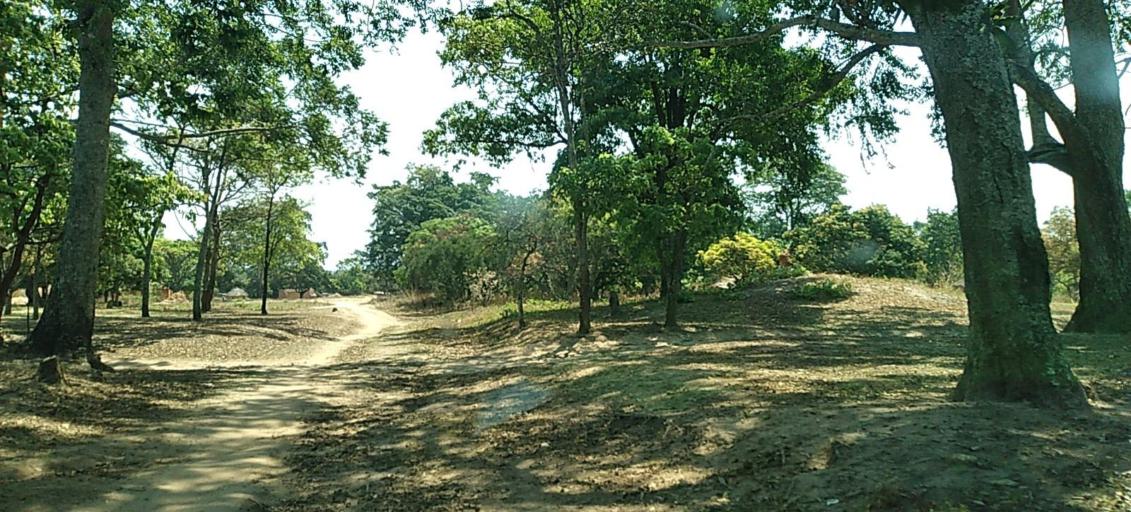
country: CD
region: Katanga
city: Kolwezi
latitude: -11.2817
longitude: 25.1494
